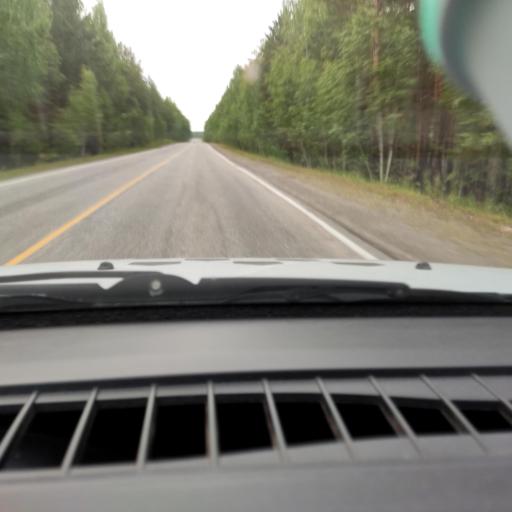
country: RU
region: Chelyabinsk
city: Ozersk
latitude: 55.8143
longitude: 60.6382
